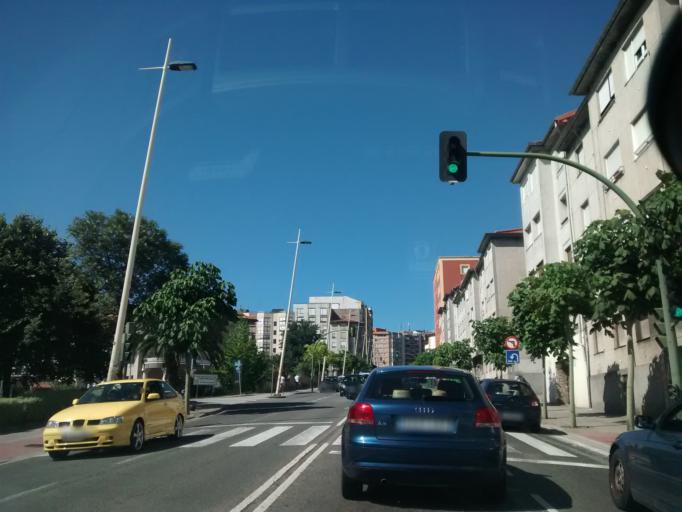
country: ES
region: Cantabria
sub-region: Provincia de Cantabria
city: Santander
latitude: 43.4555
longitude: -3.8273
